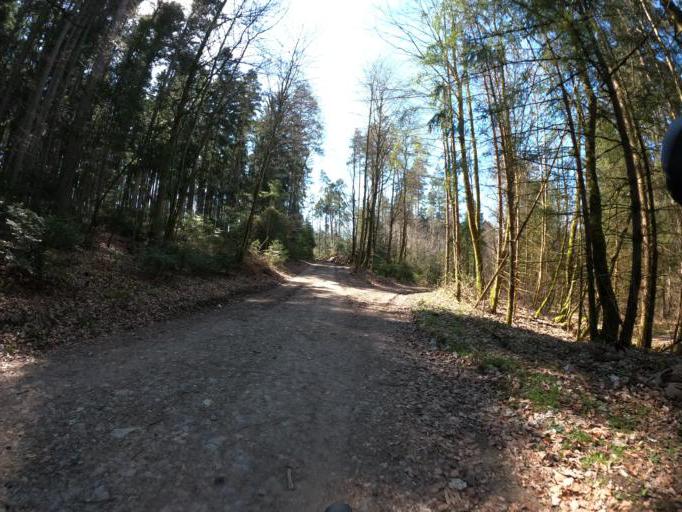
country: DE
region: Baden-Wuerttemberg
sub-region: Tuebingen Region
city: Haigerloch
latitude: 48.4194
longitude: 8.7757
